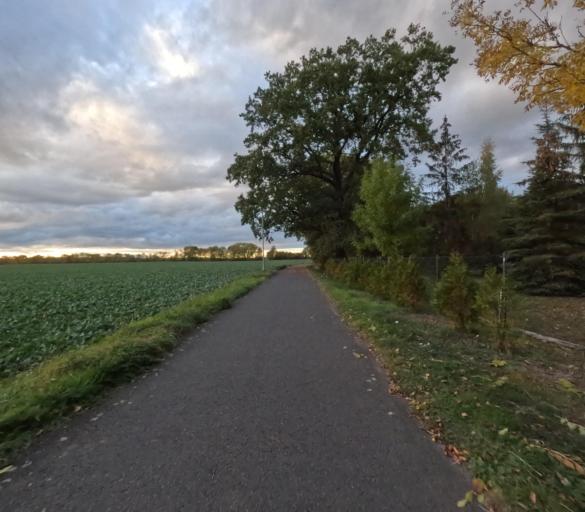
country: DE
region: Saxony
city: Naunhof
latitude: 51.2855
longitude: 12.5779
